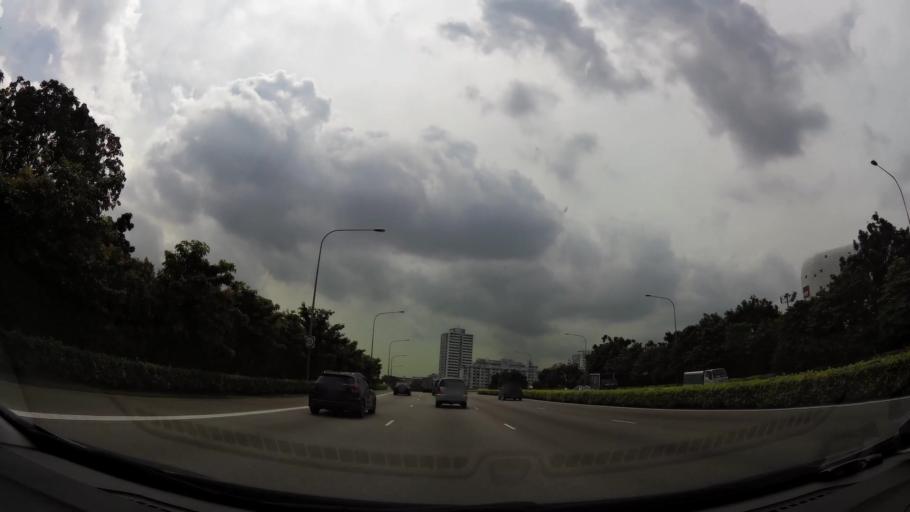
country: SG
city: Singapore
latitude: 1.3778
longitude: 103.8585
